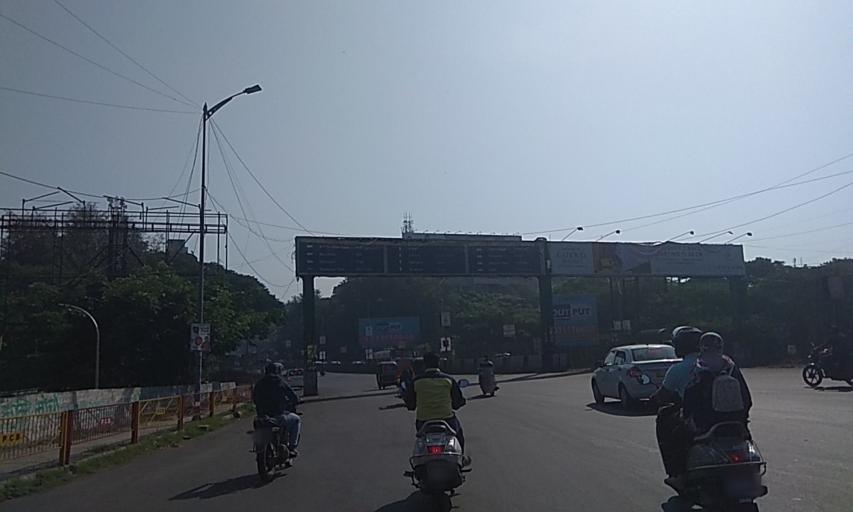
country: IN
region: Maharashtra
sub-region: Pune Division
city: Pune
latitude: 18.5068
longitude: 73.8985
